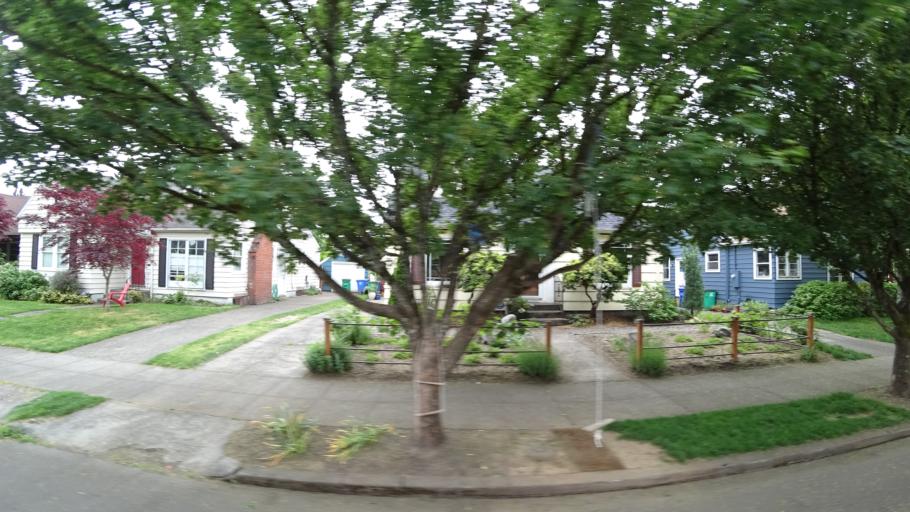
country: US
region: Oregon
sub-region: Multnomah County
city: Portland
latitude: 45.5503
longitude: -122.6221
